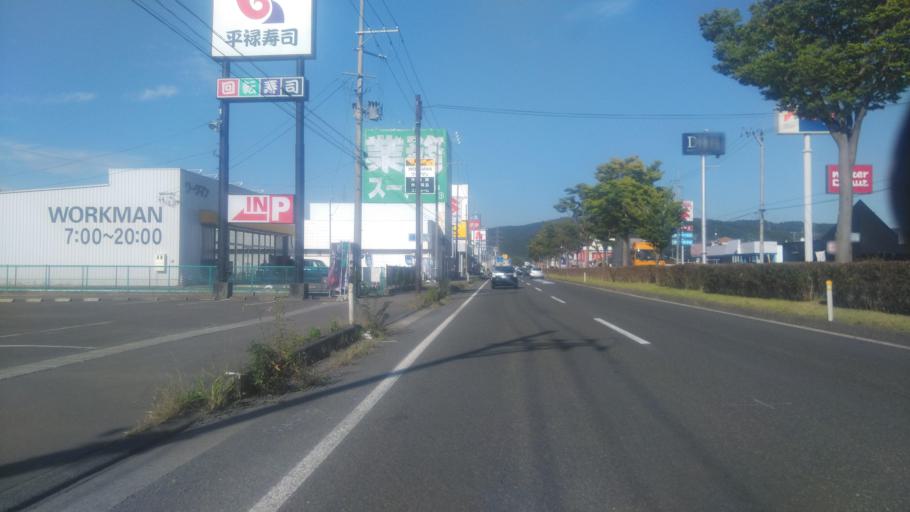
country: JP
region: Miyagi
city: Okawara
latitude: 38.0557
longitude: 140.7331
